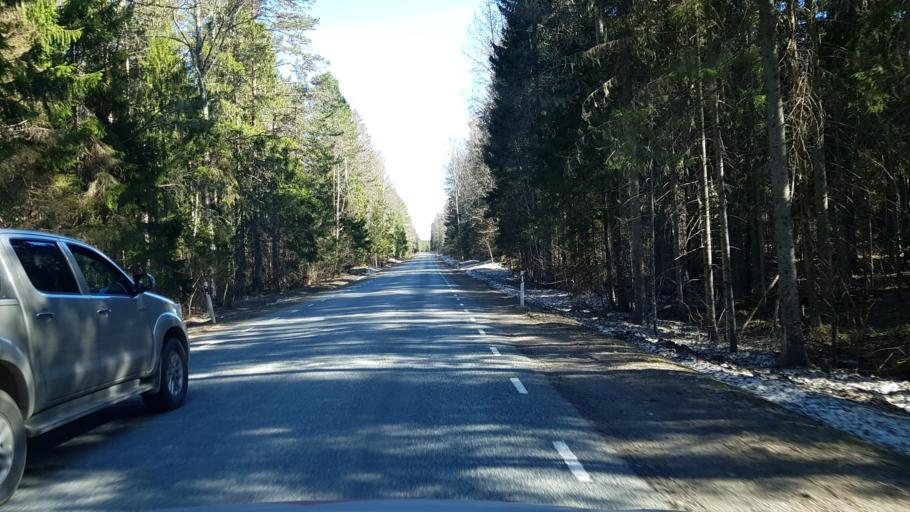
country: EE
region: Laeaene-Virumaa
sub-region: Vinni vald
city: Vinni
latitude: 59.2684
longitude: 26.6670
